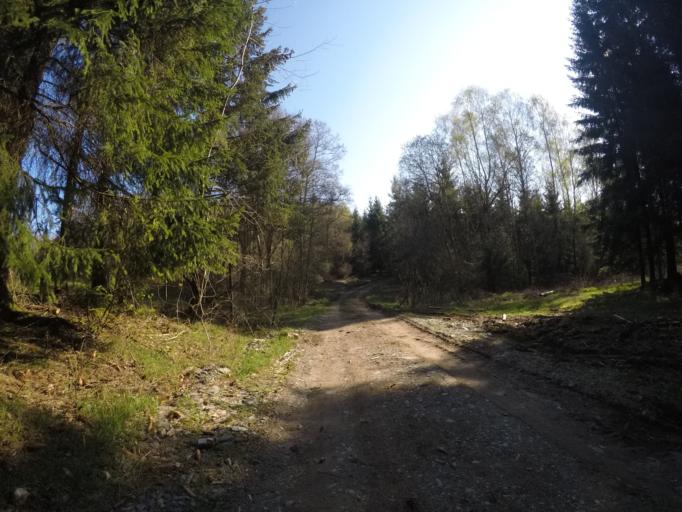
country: BE
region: Wallonia
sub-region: Province du Luxembourg
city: Leglise
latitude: 49.7823
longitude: 5.5768
